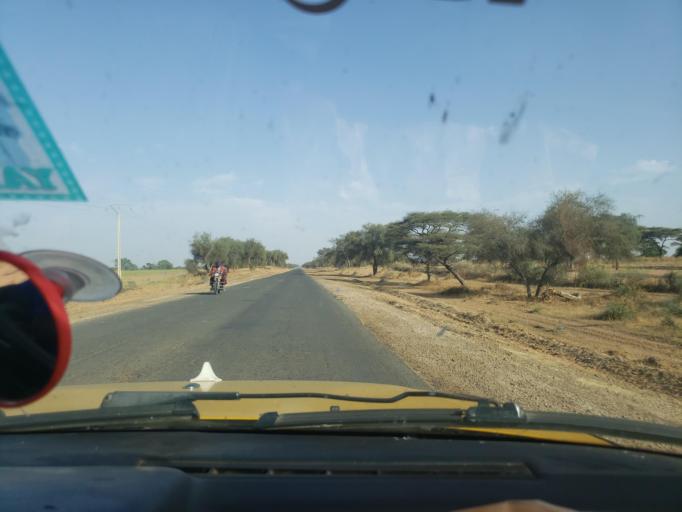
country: SN
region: Louga
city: Louga
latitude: 15.5079
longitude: -15.9716
